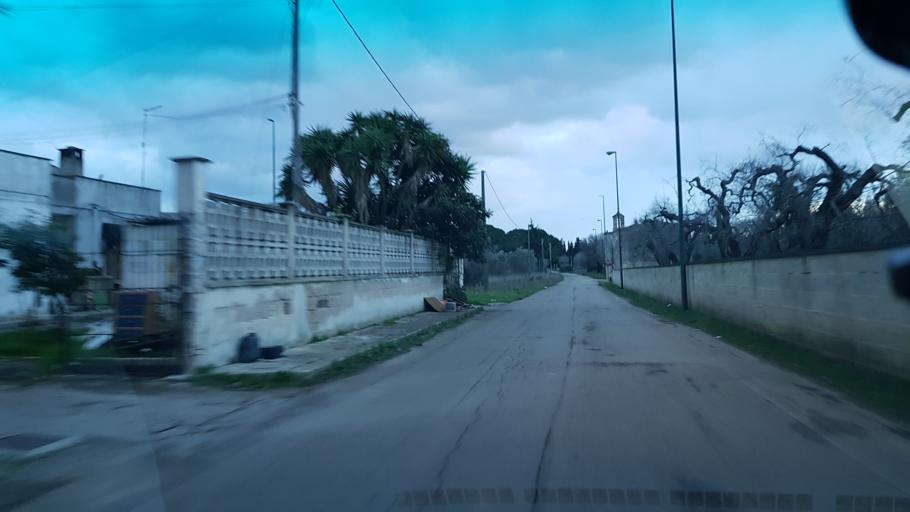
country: IT
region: Apulia
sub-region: Provincia di Brindisi
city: Torchiarolo
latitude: 40.4958
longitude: 18.0551
